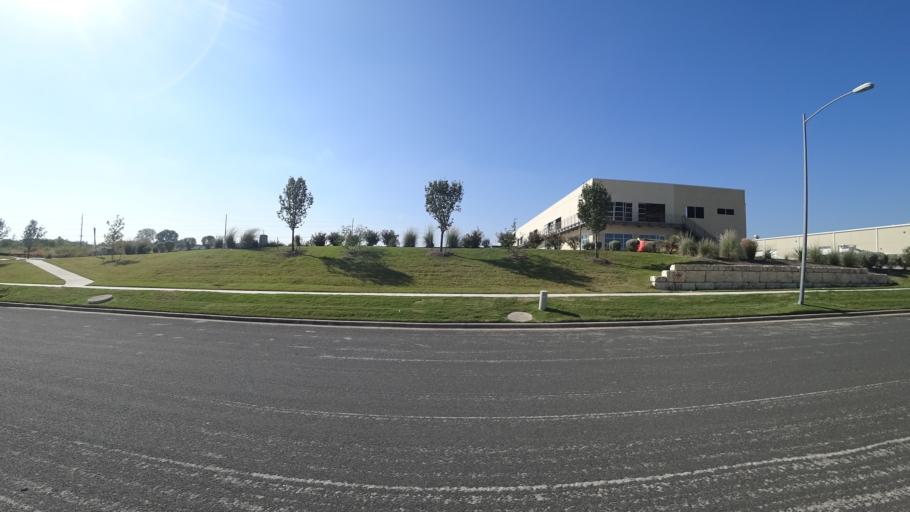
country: US
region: Texas
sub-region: Travis County
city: Austin
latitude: 30.3429
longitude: -97.6844
